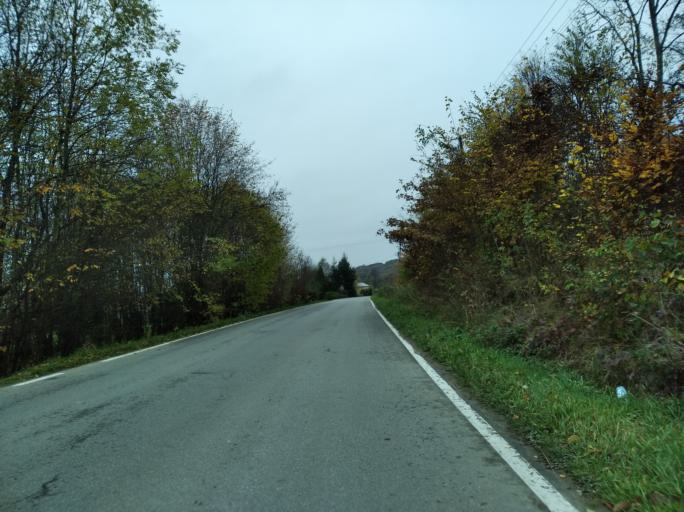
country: PL
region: Subcarpathian Voivodeship
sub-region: Powiat krosnienski
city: Leki
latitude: 49.8183
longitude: 21.6492
